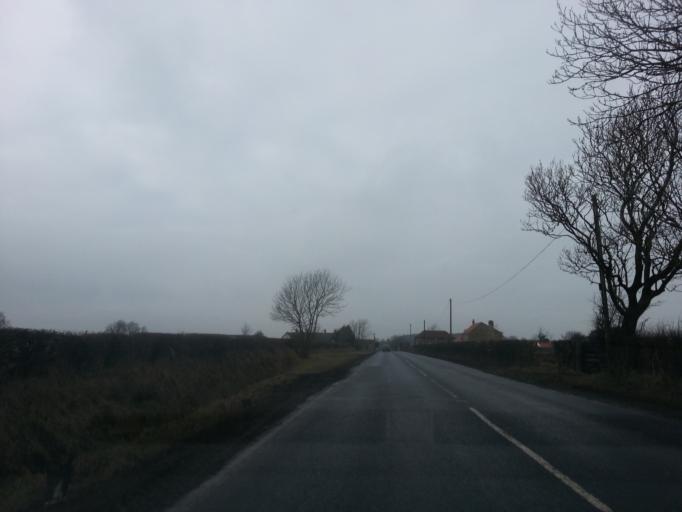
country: GB
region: England
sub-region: Darlington
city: Walworth
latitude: 54.5963
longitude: -1.6580
